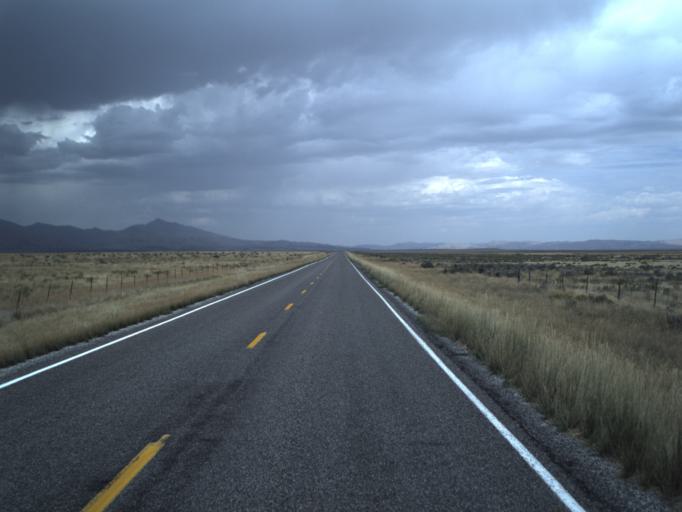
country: US
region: Idaho
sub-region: Oneida County
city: Malad City
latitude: 41.8955
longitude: -113.1092
